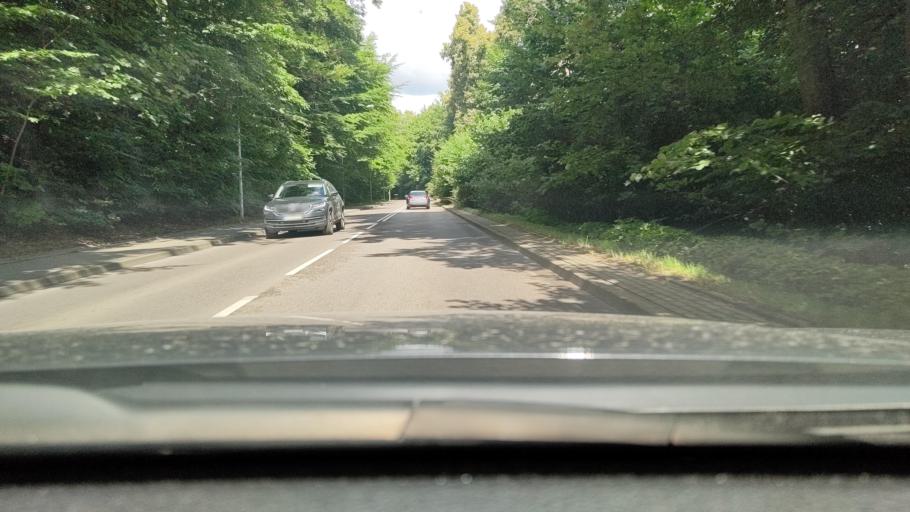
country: PL
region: Pomeranian Voivodeship
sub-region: Powiat wejherowski
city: Wejherowo
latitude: 54.5936
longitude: 18.2360
